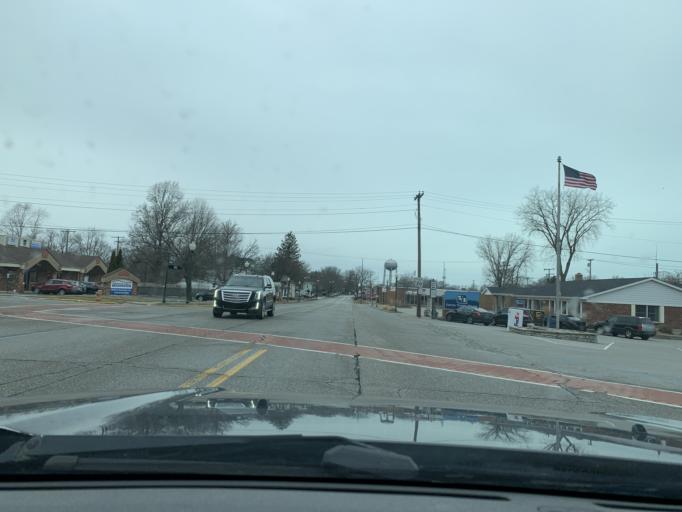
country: US
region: Indiana
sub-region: Porter County
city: Chesterton
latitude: 41.6109
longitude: -87.0542
